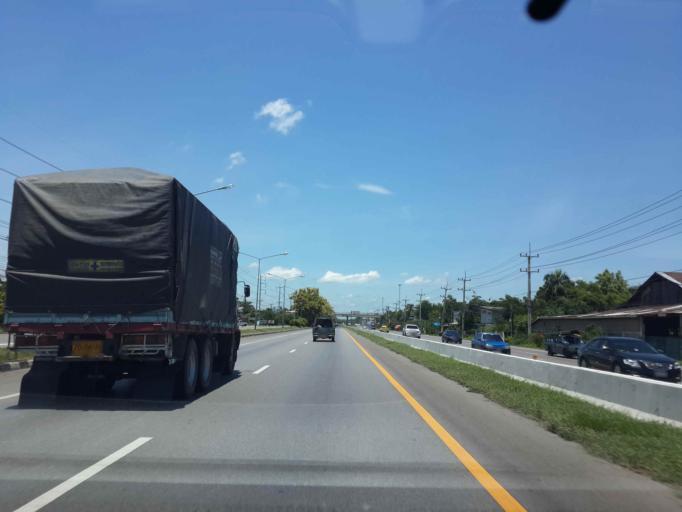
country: TH
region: Phetchaburi
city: Khao Yoi
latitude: 13.1928
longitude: 99.8321
